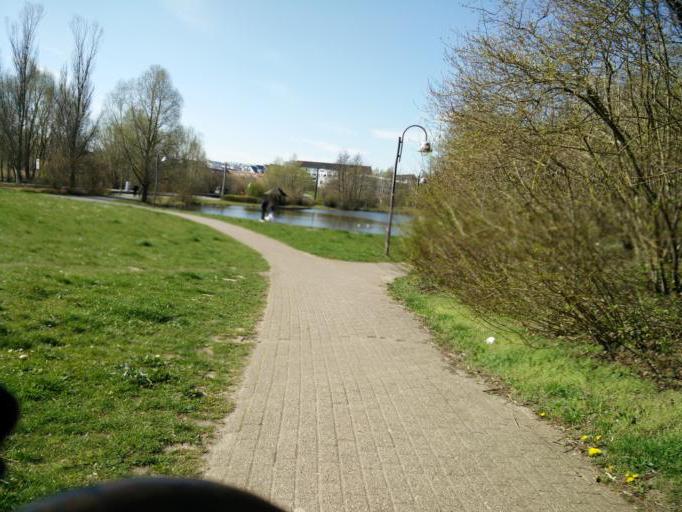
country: DE
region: Mecklenburg-Vorpommern
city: Dierkow-West
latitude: 54.1142
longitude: 12.1454
